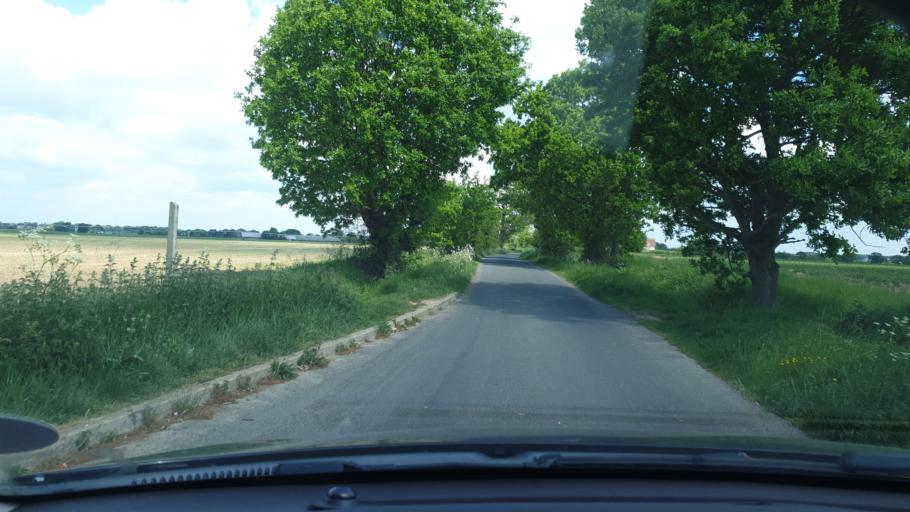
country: GB
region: England
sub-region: Essex
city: Great Bentley
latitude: 51.8434
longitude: 1.0743
